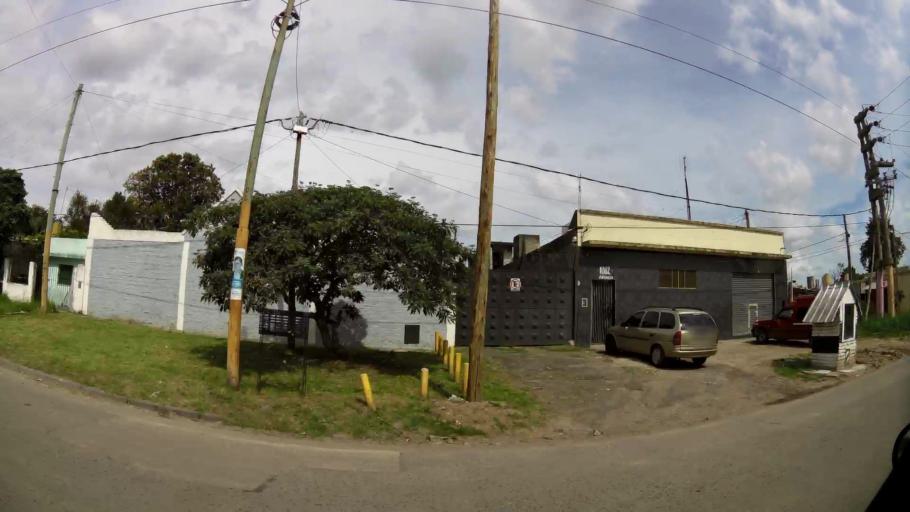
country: AR
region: Buenos Aires
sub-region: Partido de Quilmes
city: Quilmes
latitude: -34.7538
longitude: -58.2488
